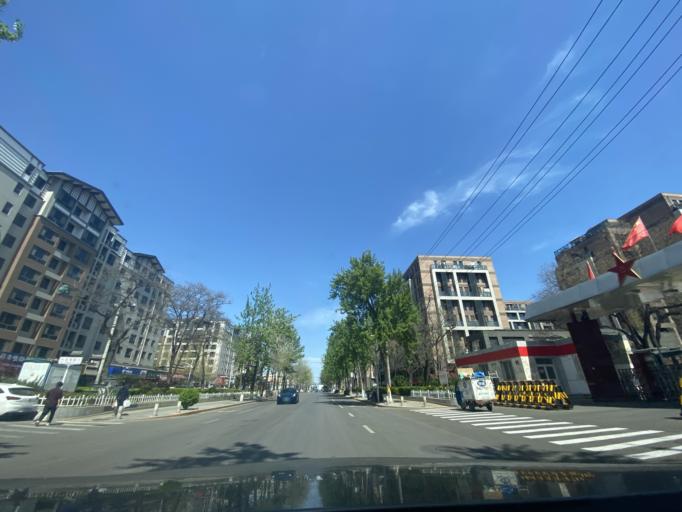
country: CN
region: Beijing
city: Sijiqing
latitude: 39.9252
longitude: 116.2587
